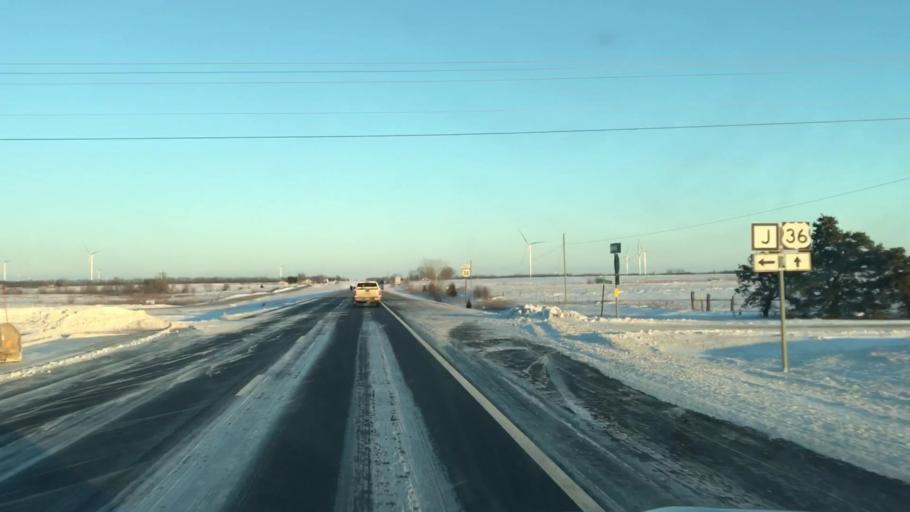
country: US
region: Missouri
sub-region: DeKalb County
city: Maysville
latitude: 39.7617
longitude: -94.4328
